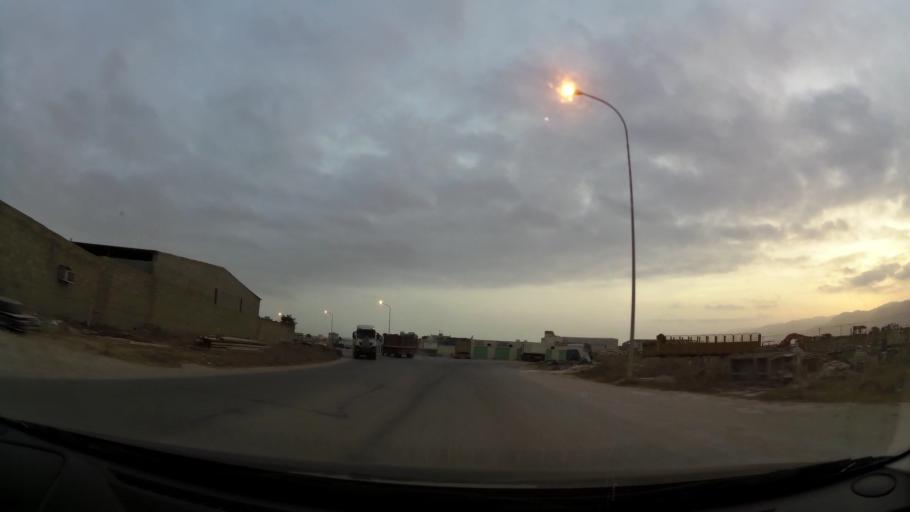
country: OM
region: Zufar
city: Salalah
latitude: 17.0317
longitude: 54.0345
